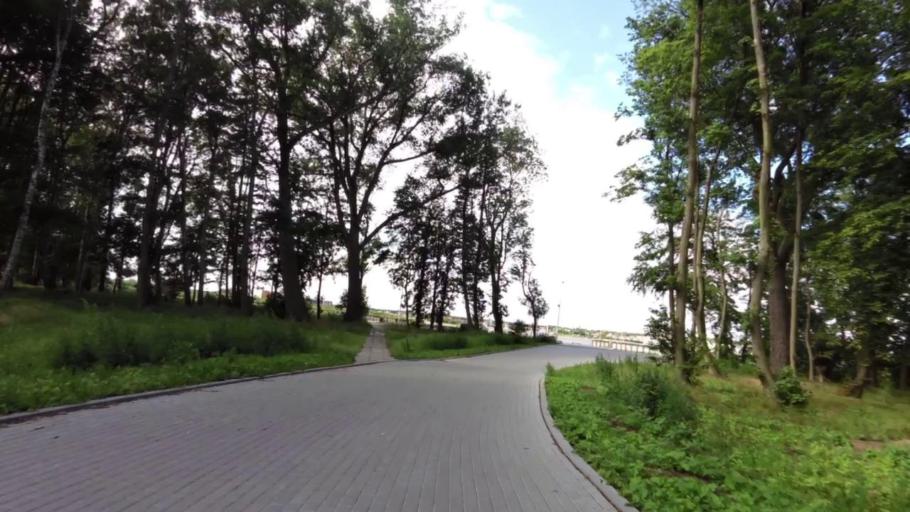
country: PL
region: West Pomeranian Voivodeship
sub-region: Powiat slawienski
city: Darlowo
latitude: 54.4351
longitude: 16.3900
